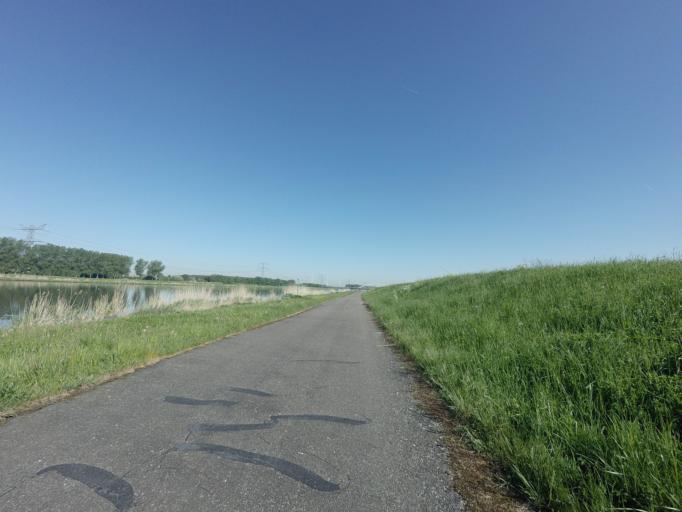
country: NL
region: North Brabant
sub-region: Gemeente Woensdrecht
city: Woensdrecht
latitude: 51.3920
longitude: 4.2442
